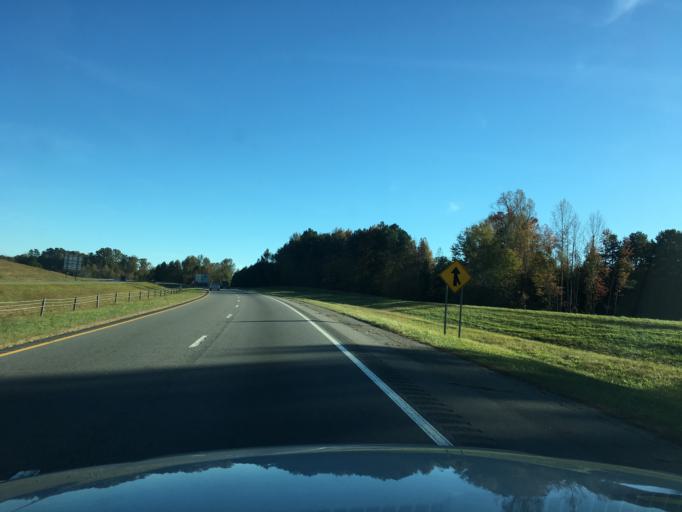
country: US
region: North Carolina
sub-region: Catawba County
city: Mountain View
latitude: 35.6930
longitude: -81.3524
